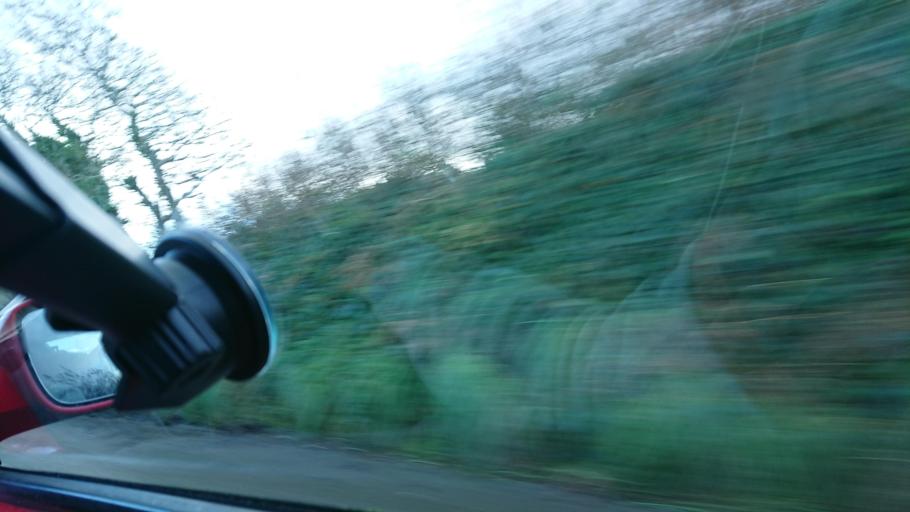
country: GB
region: England
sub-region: Cornwall
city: Looe
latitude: 50.3484
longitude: -4.4775
